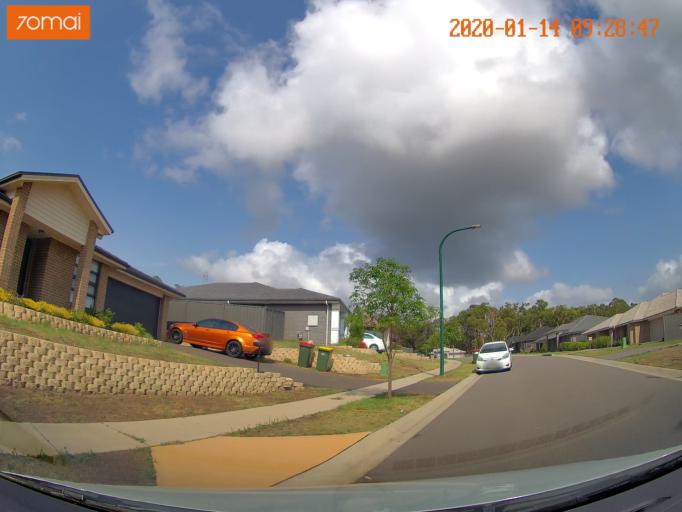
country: AU
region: New South Wales
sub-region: Lake Macquarie Shire
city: Dora Creek
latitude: -33.1200
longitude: 151.5296
